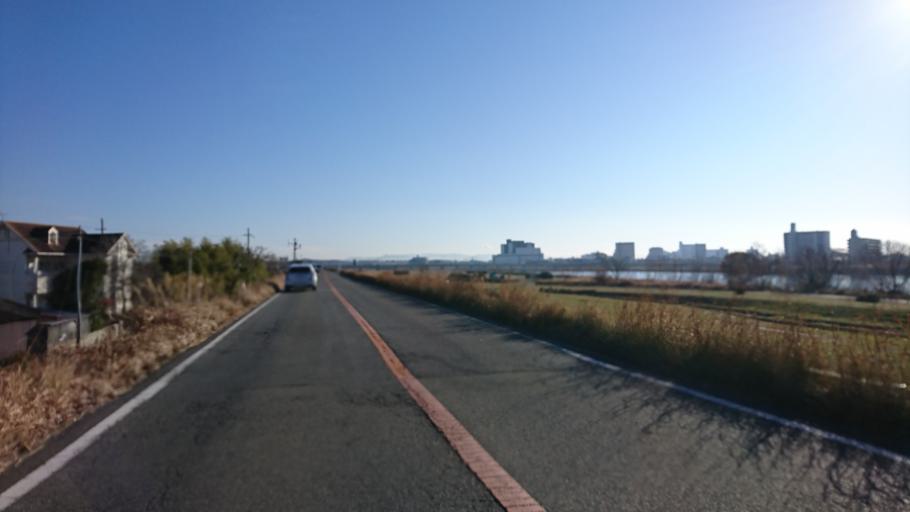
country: JP
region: Hyogo
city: Kakogawacho-honmachi
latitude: 34.7732
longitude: 134.8201
